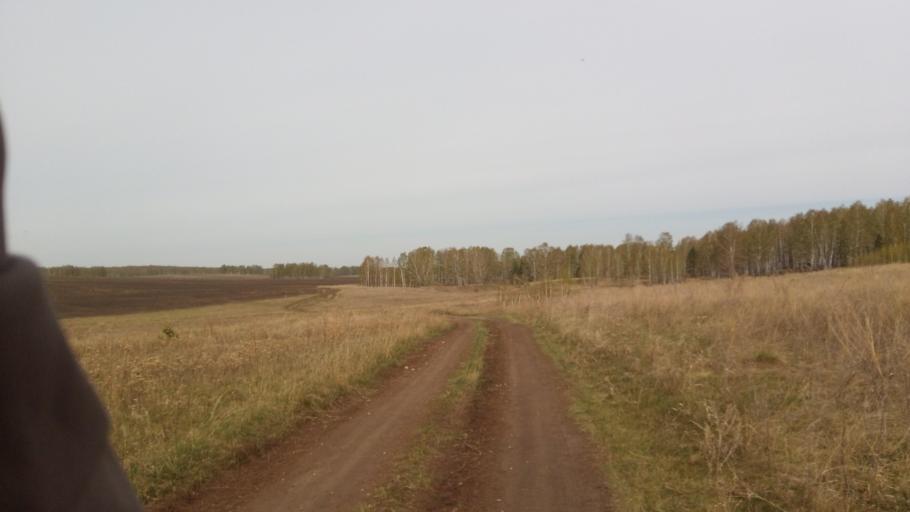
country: RU
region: Chelyabinsk
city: Timiryazevskiy
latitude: 55.0132
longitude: 60.8618
